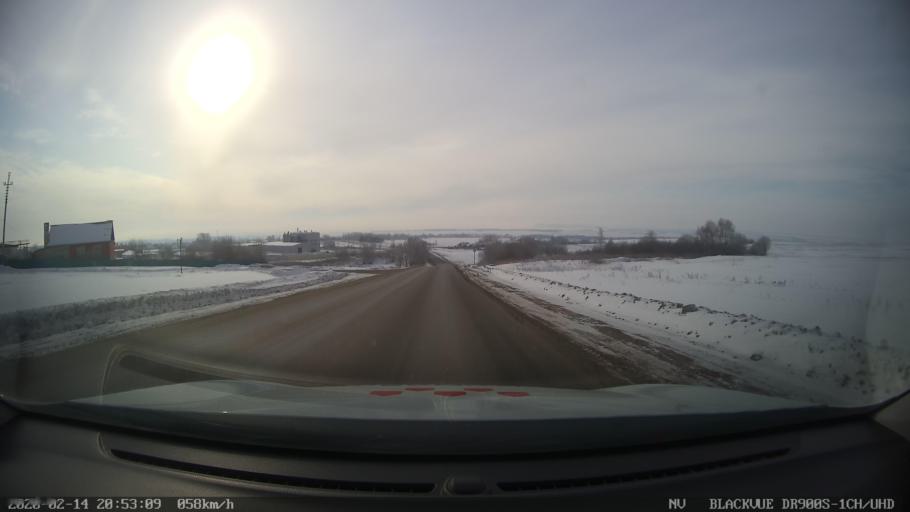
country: RU
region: Tatarstan
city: Kuybyshevskiy Zaton
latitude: 55.1975
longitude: 49.2482
